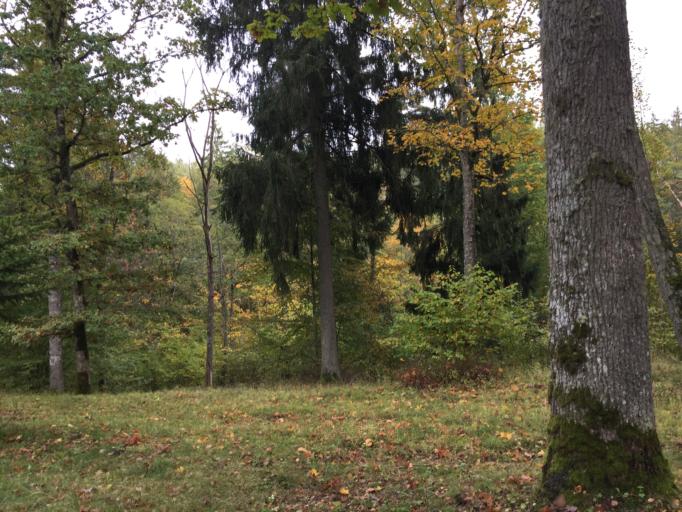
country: LV
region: Auces Novads
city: Auce
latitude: 56.5498
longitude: 23.0183
